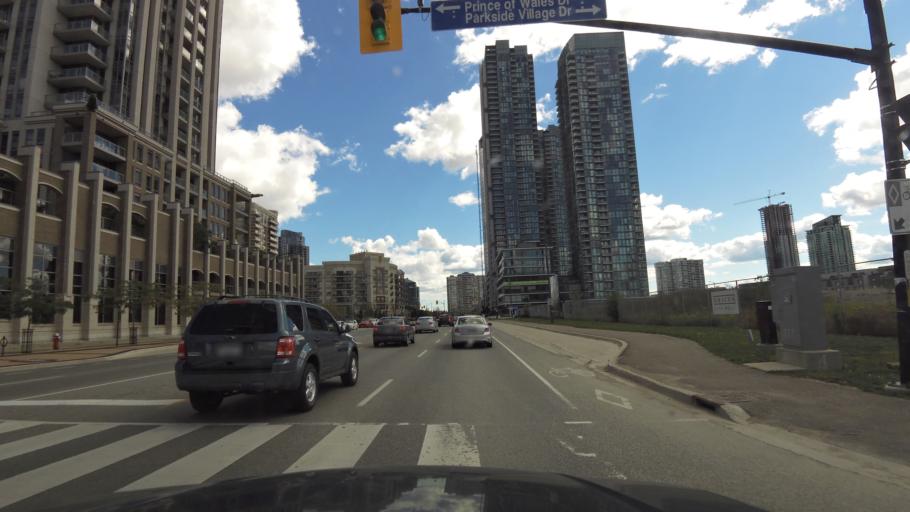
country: CA
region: Ontario
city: Mississauga
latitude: 43.5881
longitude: -79.6492
